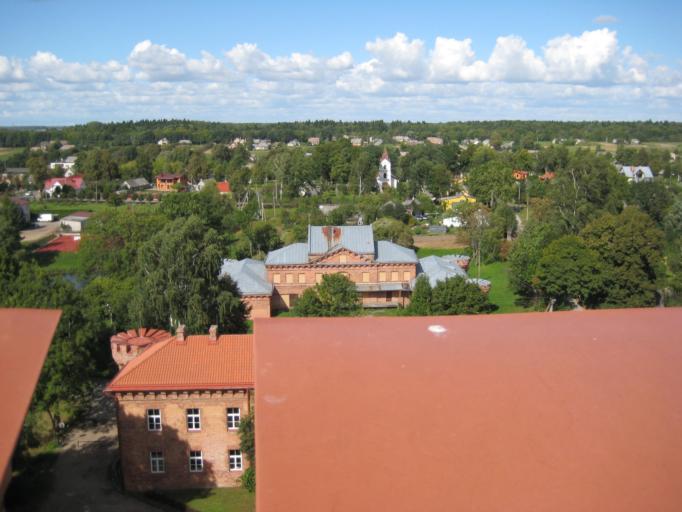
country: LT
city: Gelgaudiskis
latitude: 55.0964
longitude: 23.1306
